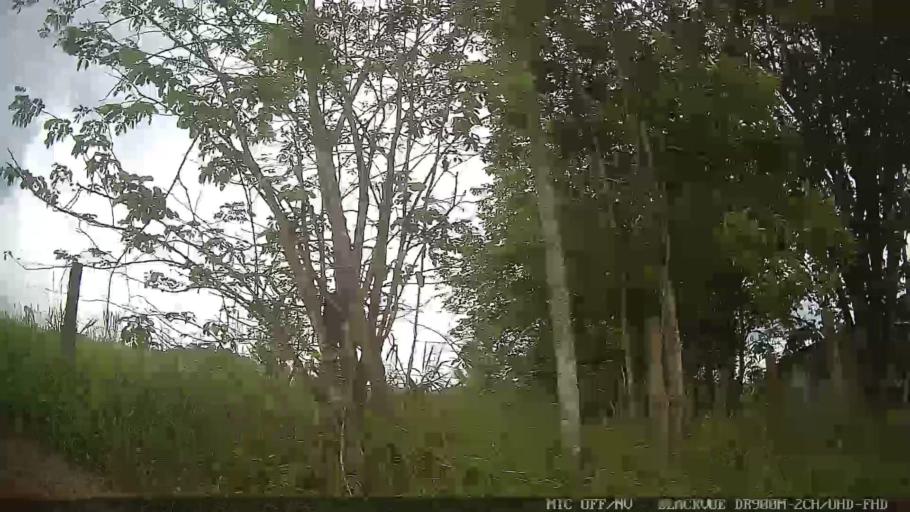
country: BR
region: Sao Paulo
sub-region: Aruja
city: Aruja
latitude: -23.4111
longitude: -46.2305
